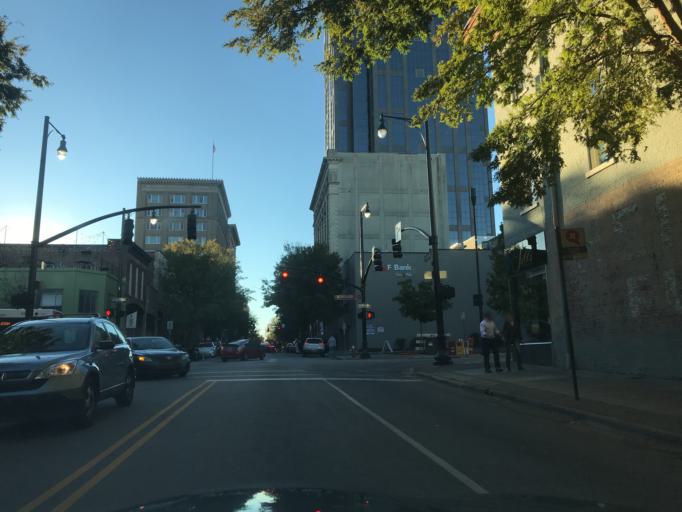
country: US
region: North Carolina
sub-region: Wake County
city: Raleigh
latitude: 35.7782
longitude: -78.6379
